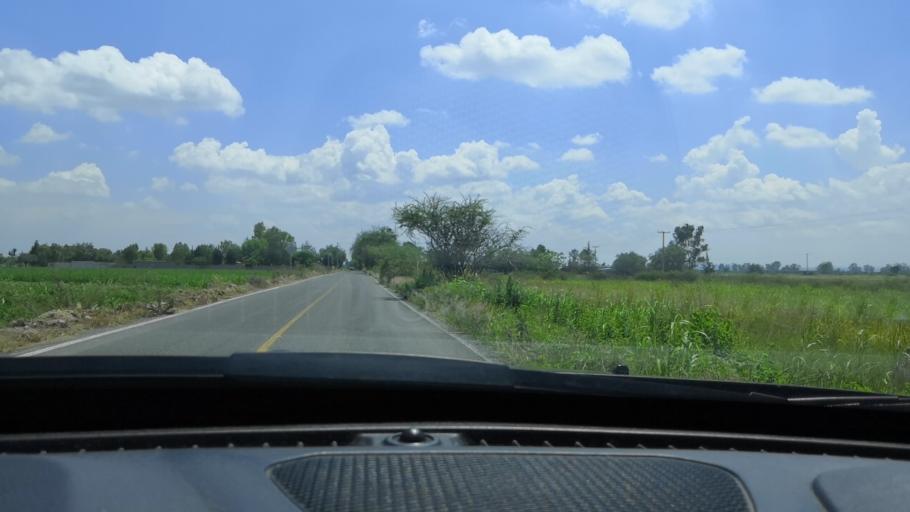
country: MX
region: Guanajuato
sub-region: Silao de la Victoria
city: El Refugio de los Sauces
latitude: 20.9528
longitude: -101.6005
